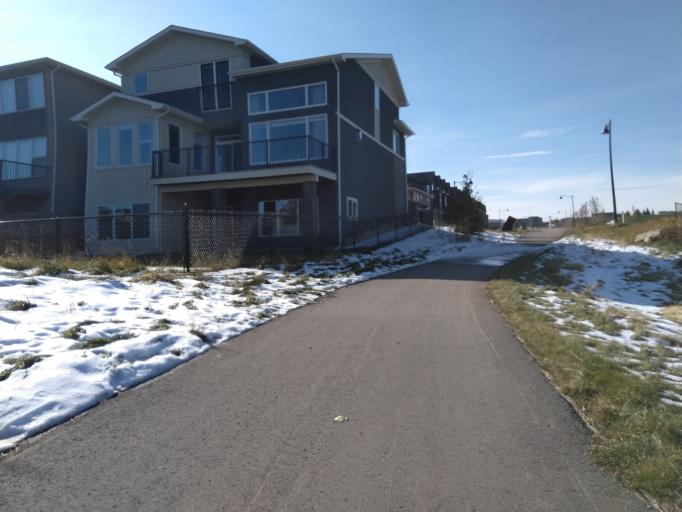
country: CA
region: Alberta
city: Calgary
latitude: 51.1758
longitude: -114.1291
